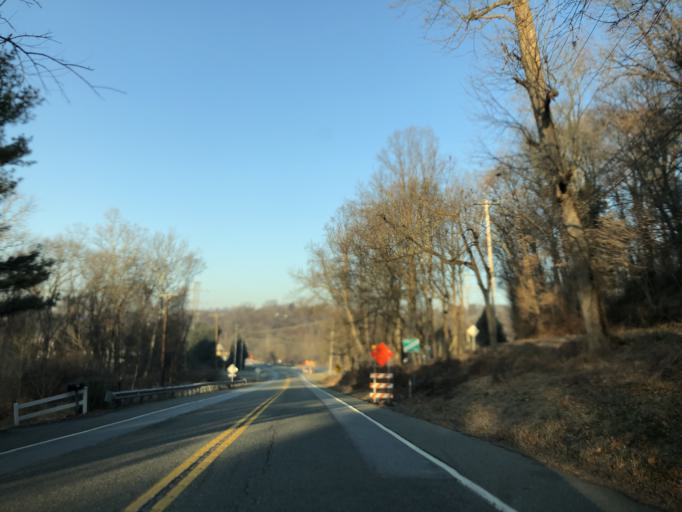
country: US
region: Pennsylvania
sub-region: Chester County
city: West Chester
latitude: 39.9687
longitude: -75.6613
